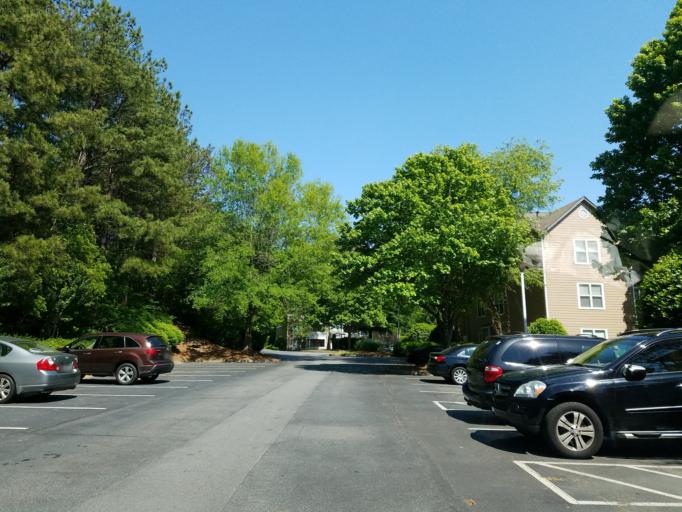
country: US
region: Georgia
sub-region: Cobb County
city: Marietta
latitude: 33.9666
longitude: -84.4884
